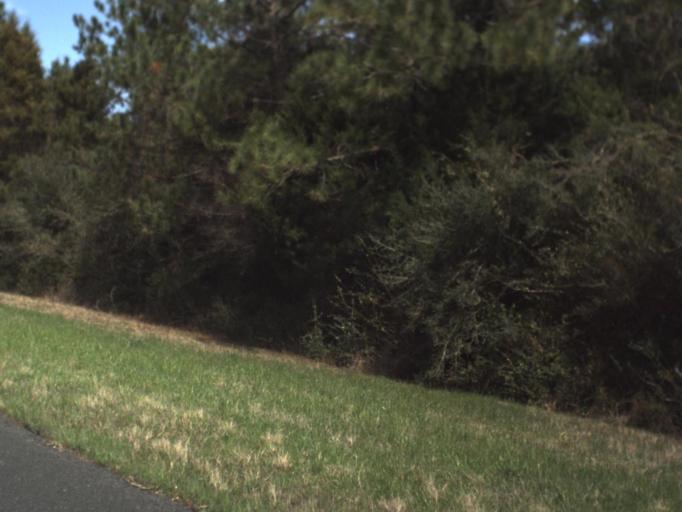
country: US
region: Florida
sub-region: Bay County
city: Youngstown
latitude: 30.5949
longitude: -85.3960
